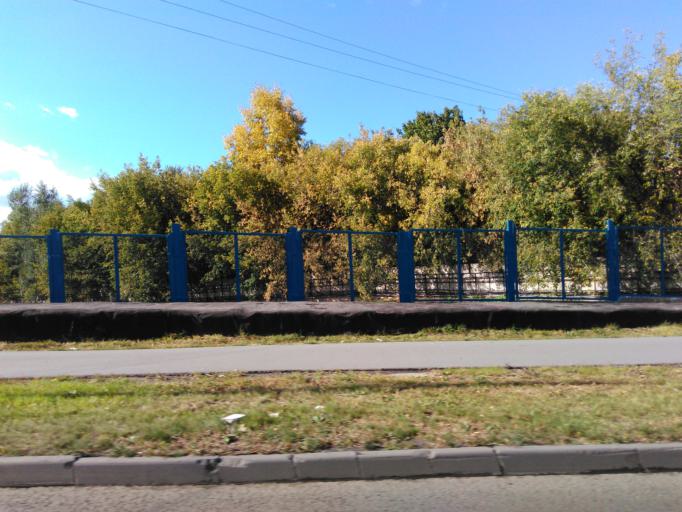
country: RU
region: Moscow
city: Otradnoye
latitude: 55.8529
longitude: 37.6054
